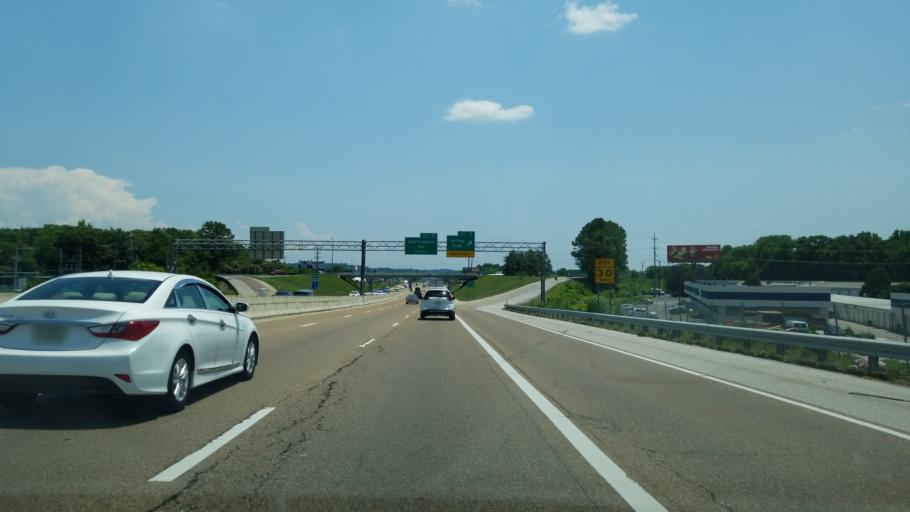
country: US
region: Tennessee
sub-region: Hamilton County
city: East Chattanooga
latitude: 35.0676
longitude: -85.1960
